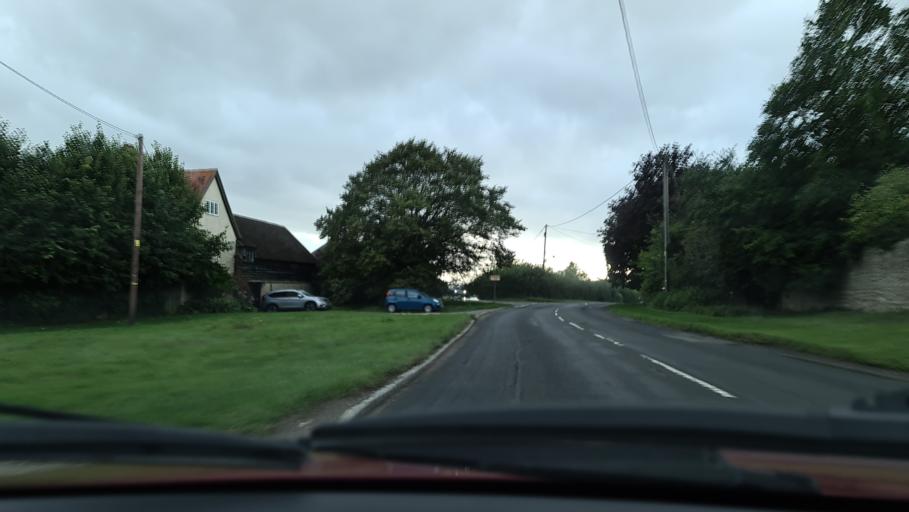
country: GB
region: England
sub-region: Buckinghamshire
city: Long Crendon
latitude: 51.7773
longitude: -1.0060
